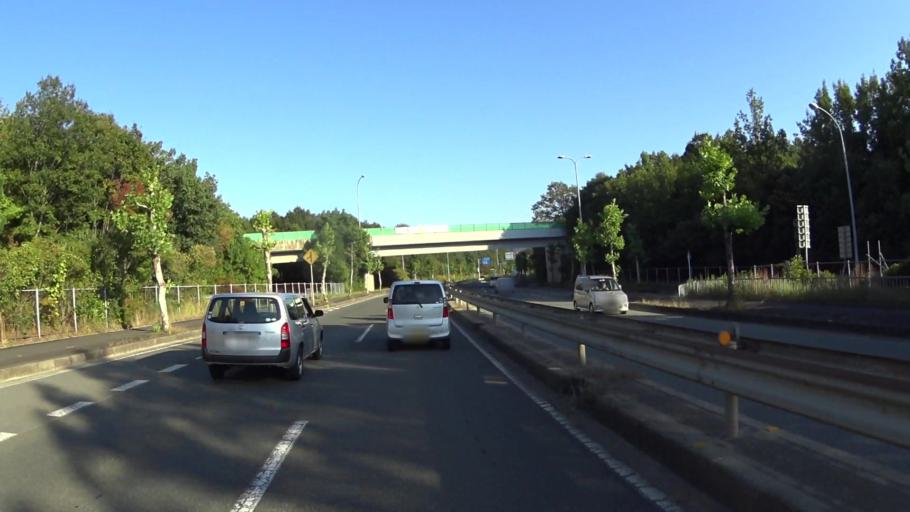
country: JP
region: Kyoto
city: Fukuchiyama
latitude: 35.2865
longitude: 135.1791
